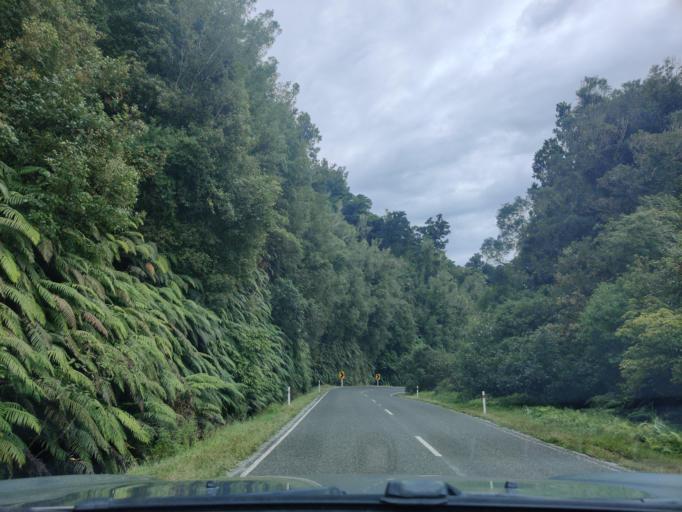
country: NZ
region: West Coast
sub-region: Westland District
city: Hokitika
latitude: -43.1593
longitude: 170.4771
